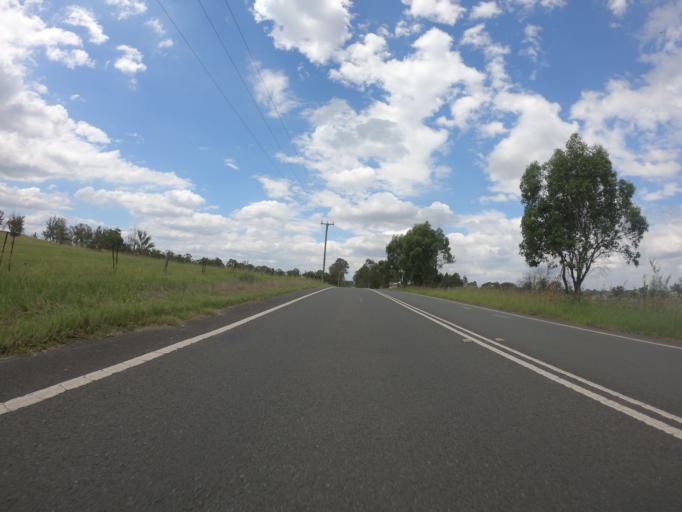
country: AU
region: New South Wales
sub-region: Liverpool
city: Luddenham
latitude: -33.8385
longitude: 150.7473
